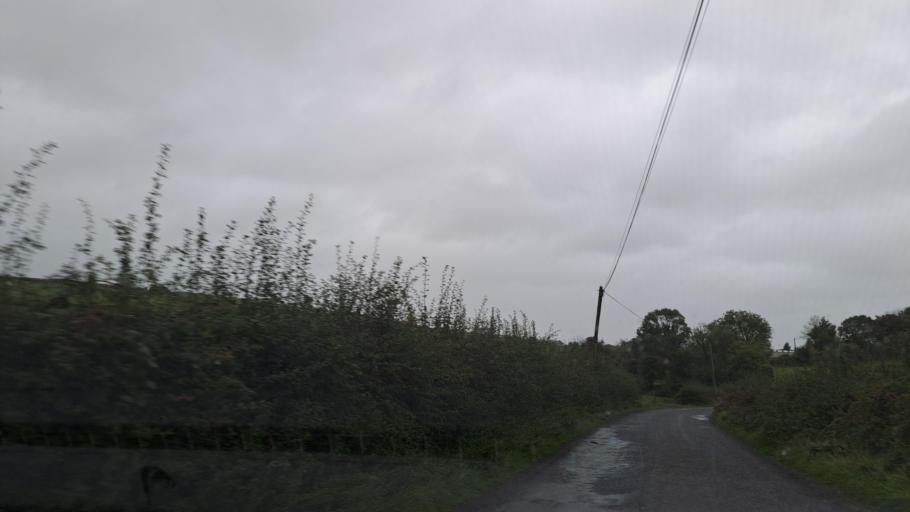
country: IE
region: Ulster
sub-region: An Cabhan
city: Kingscourt
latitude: 54.0075
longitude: -6.8212
